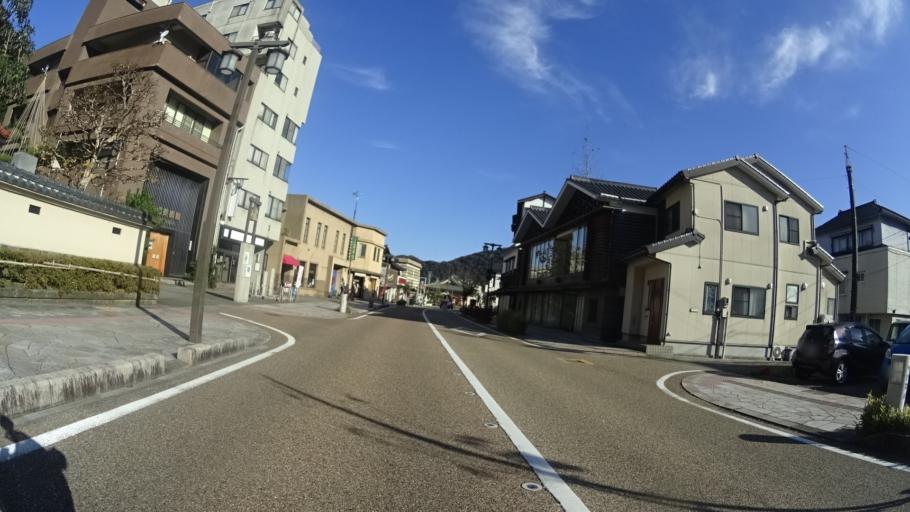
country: JP
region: Fukui
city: Maruoka
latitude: 36.2458
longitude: 136.3730
